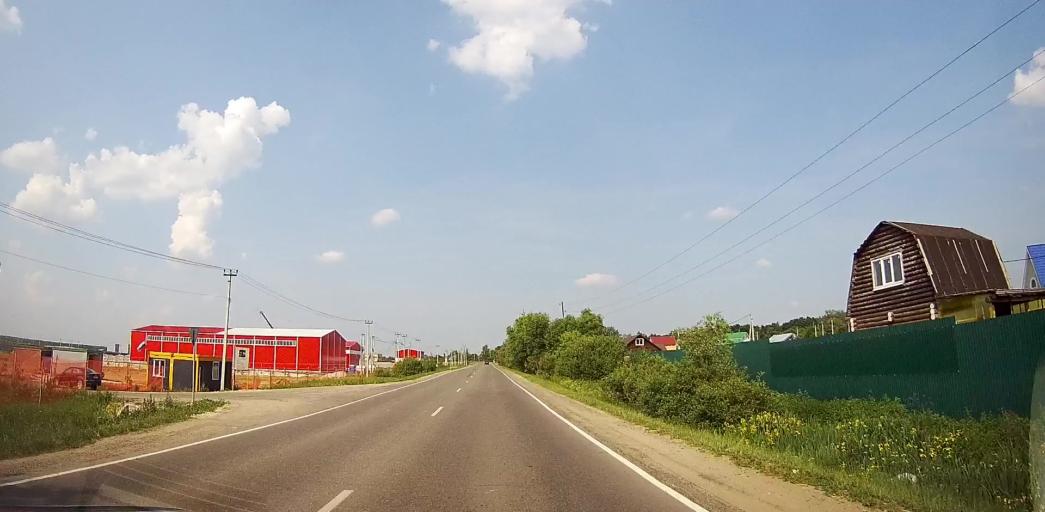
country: RU
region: Moskovskaya
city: Mikhnevo
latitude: 55.1527
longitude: 37.9564
